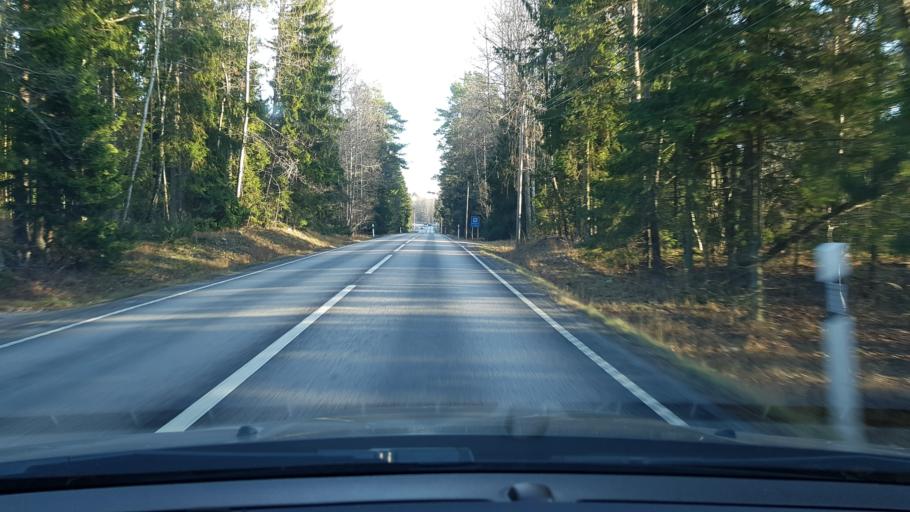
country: SE
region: Stockholm
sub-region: Norrtalje Kommun
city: Rimbo
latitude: 59.7400
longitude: 18.3250
